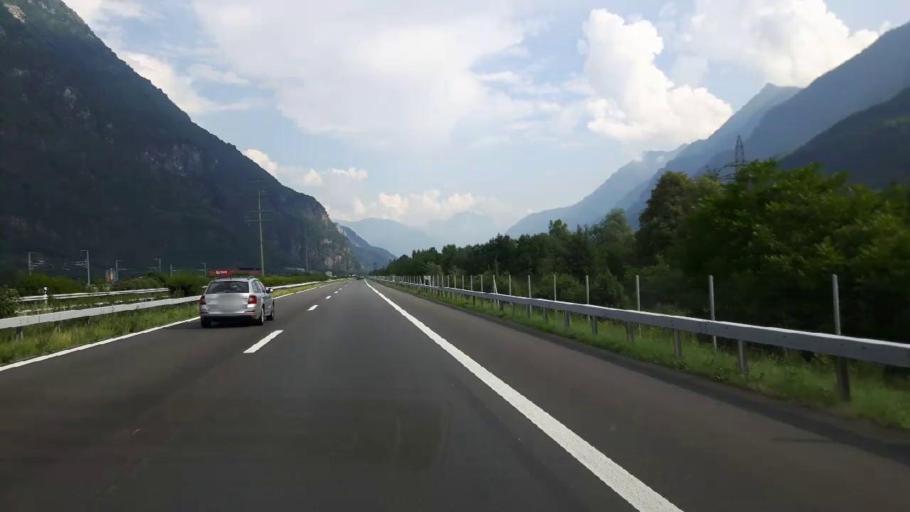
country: CH
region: Ticino
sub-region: Riviera District
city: Biasca
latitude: 46.3437
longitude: 8.9676
